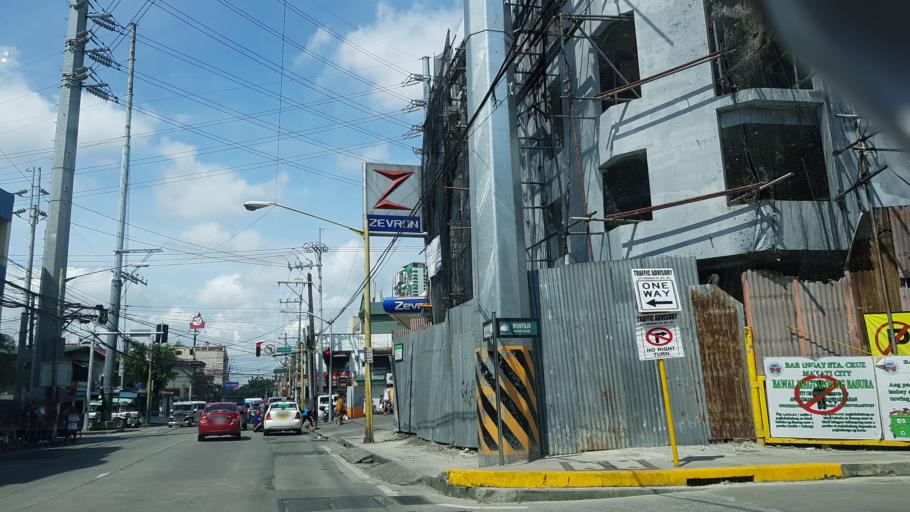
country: PH
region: Metro Manila
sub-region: Makati City
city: Makati City
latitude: 14.5701
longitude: 121.0147
